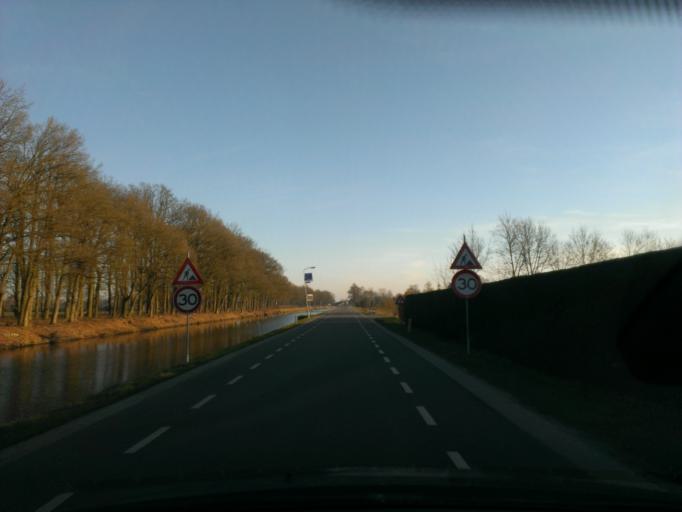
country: NL
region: Gelderland
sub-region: Gemeente Heerde
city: Heerde
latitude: 52.3933
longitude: 6.0592
